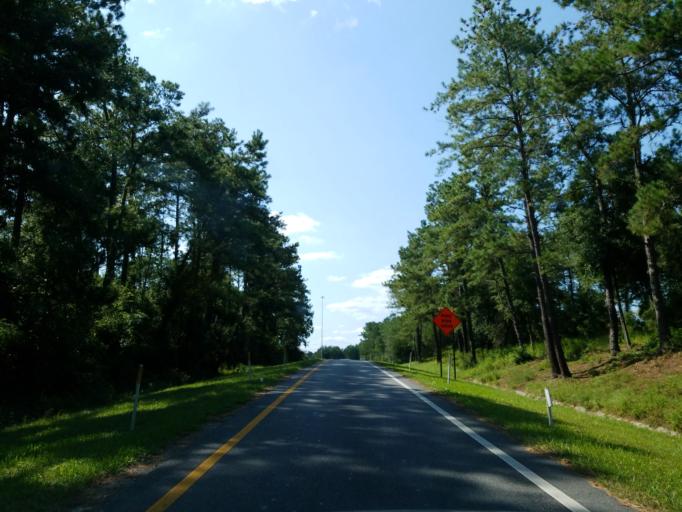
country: US
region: Florida
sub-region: Alachua County
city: Alachua
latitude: 29.6608
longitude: -82.4182
